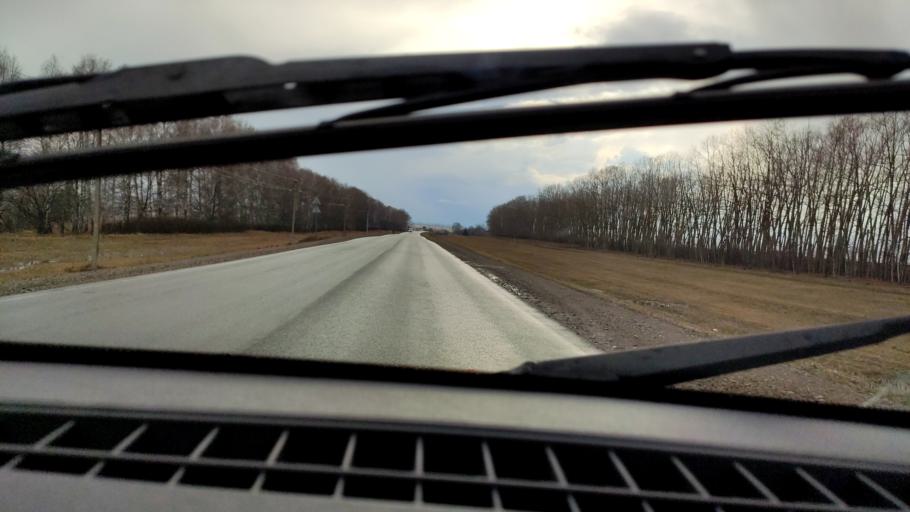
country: RU
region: Bashkortostan
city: Kushnarenkovo
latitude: 55.0558
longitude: 55.1527
